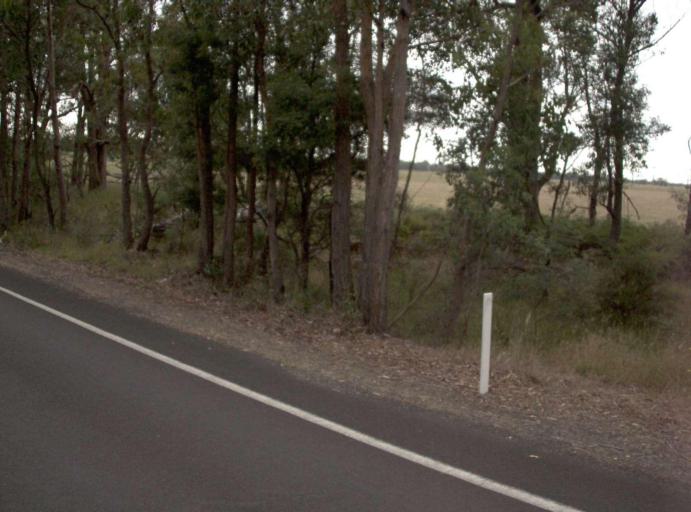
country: AU
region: Victoria
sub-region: Wellington
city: Sale
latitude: -38.4054
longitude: 146.9667
